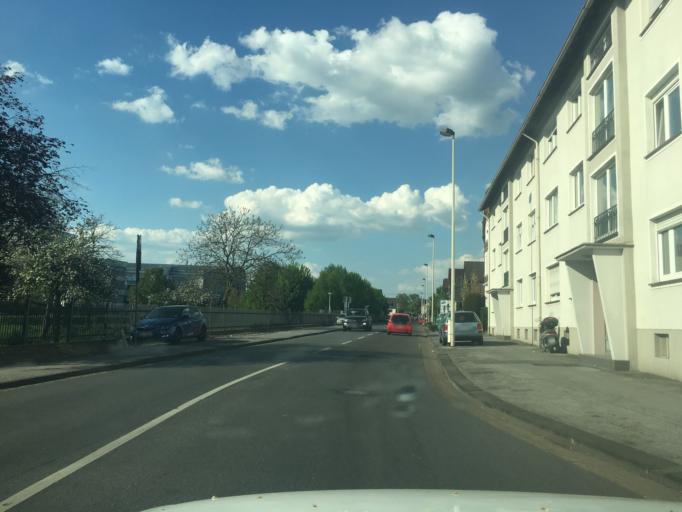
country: DE
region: North Rhine-Westphalia
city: Haan
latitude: 51.1678
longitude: 6.9850
